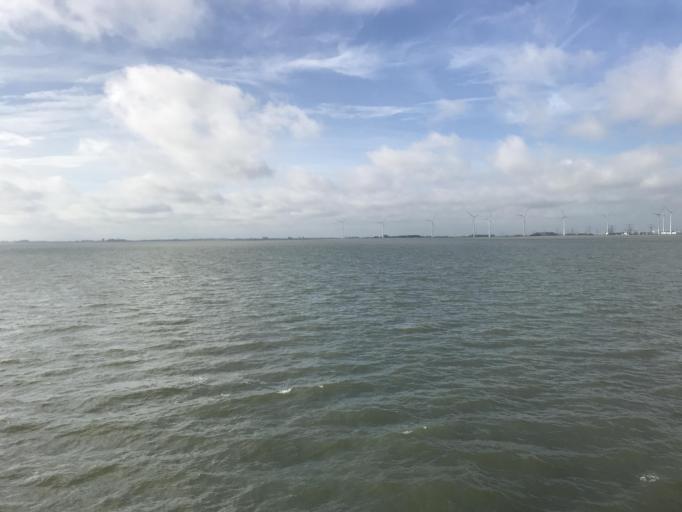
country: NL
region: Groningen
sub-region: Gemeente Delfzijl
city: Delfzijl
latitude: 53.4301
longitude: 6.9175
